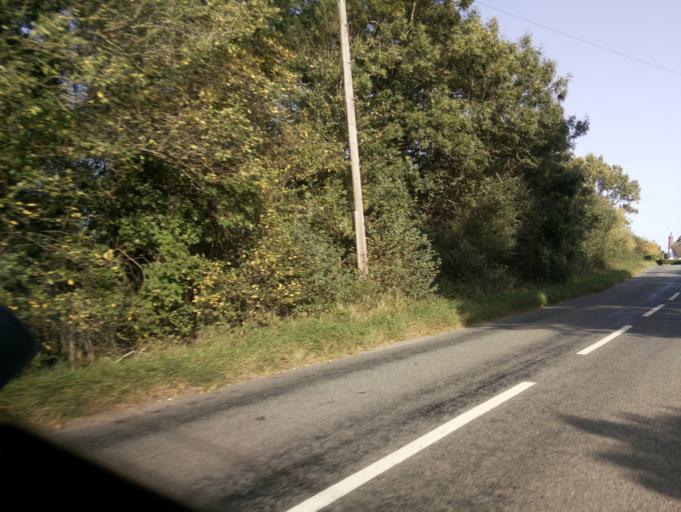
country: GB
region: England
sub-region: Gloucestershire
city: Tewkesbury
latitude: 51.9443
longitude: -2.2075
